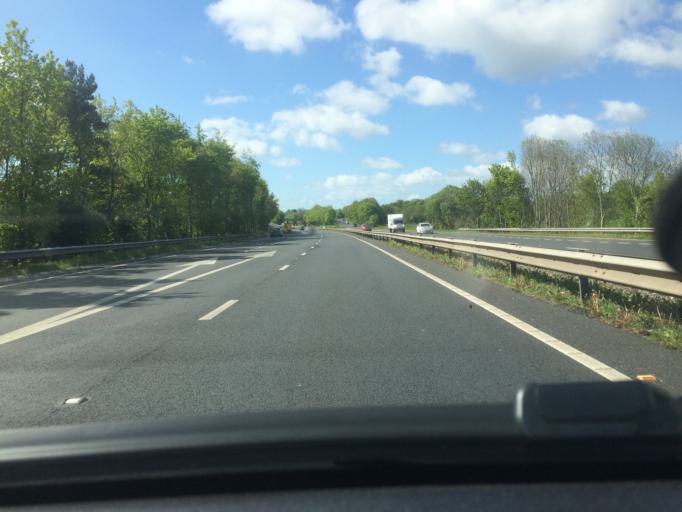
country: GB
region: Wales
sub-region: Wrexham
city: Wrexham
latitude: 53.0594
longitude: -3.0076
